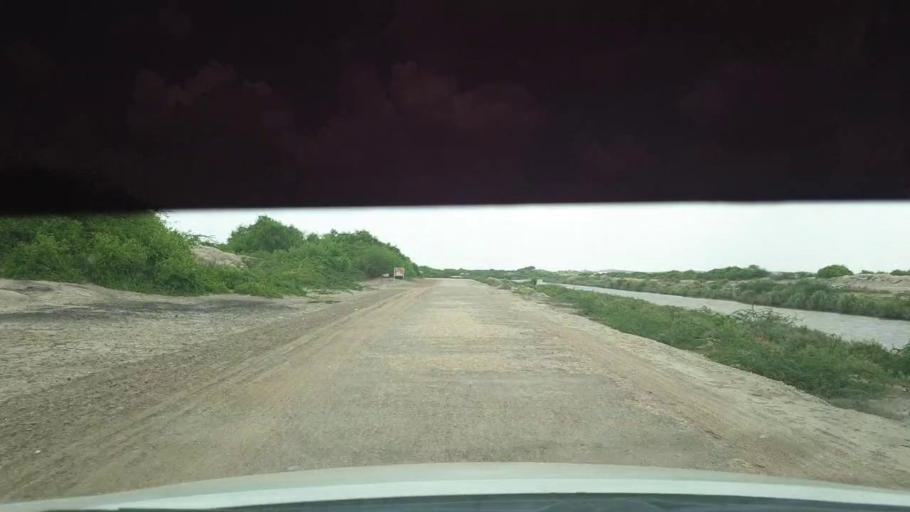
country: PK
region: Sindh
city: Kadhan
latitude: 24.4753
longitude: 69.0619
